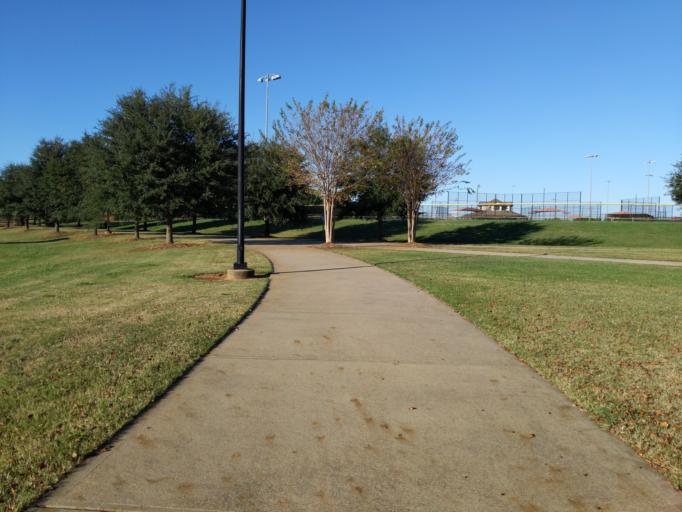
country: US
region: South Carolina
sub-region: Spartanburg County
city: Duncan
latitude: 34.8695
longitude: -82.1028
